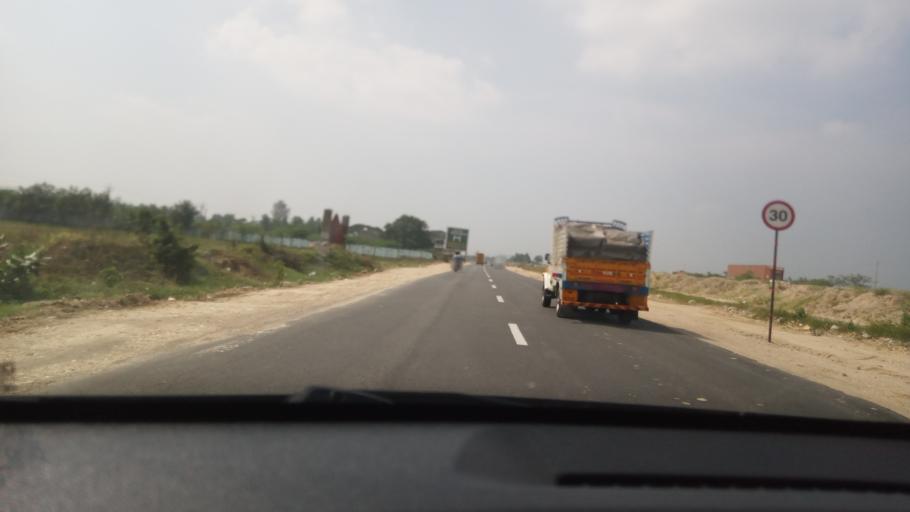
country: IN
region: Tamil Nadu
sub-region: Vellore
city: Walajapet
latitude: 12.9022
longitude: 79.4830
